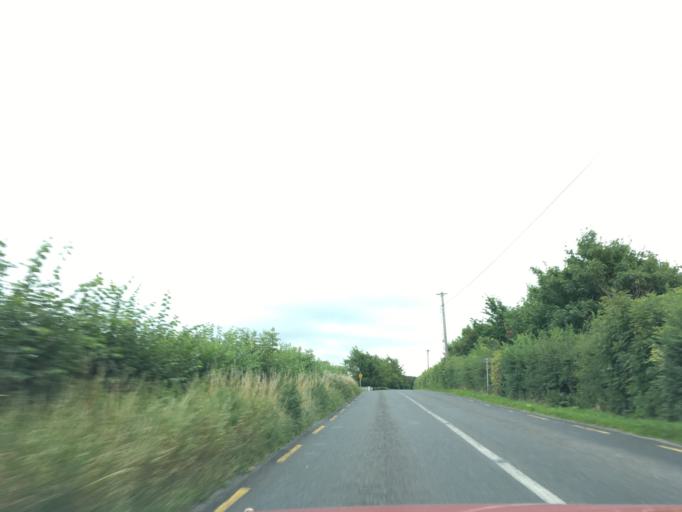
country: IE
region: Munster
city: Cashel
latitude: 52.4579
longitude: -7.8202
